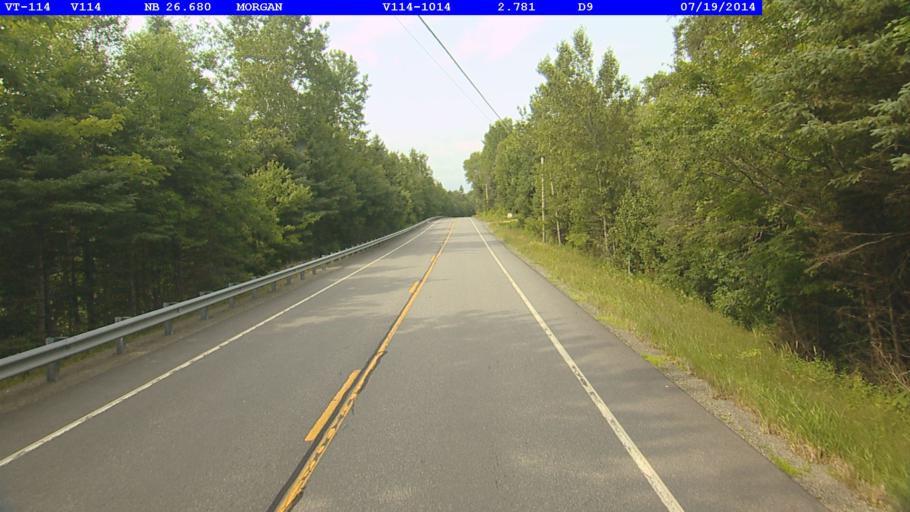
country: CA
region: Quebec
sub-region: Estrie
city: Coaticook
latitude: 44.8837
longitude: -71.8962
